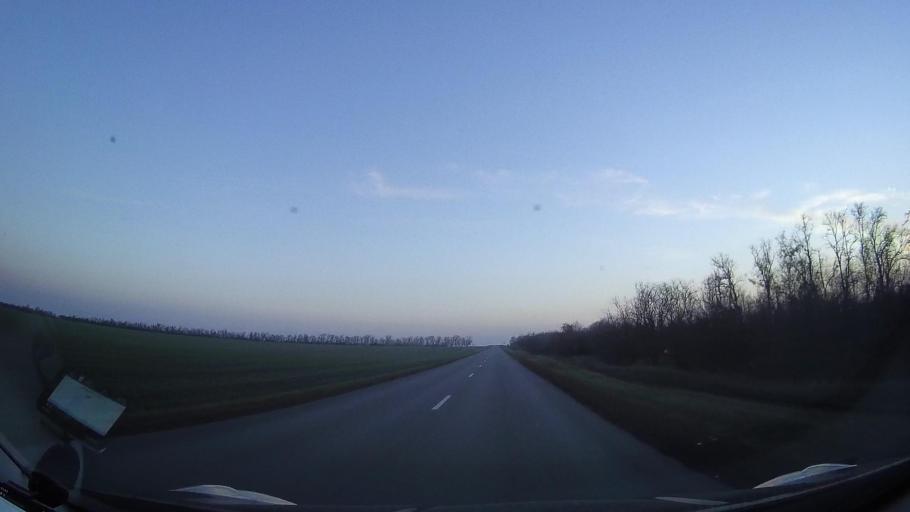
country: RU
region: Rostov
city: Zernograd
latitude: 46.9169
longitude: 40.3388
